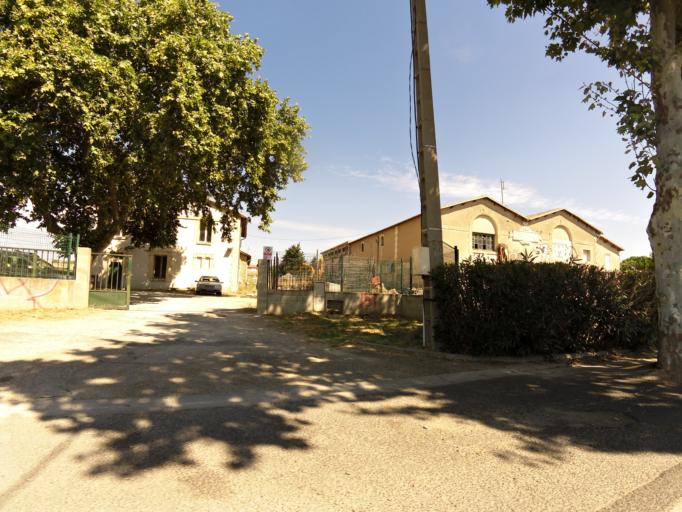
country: FR
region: Languedoc-Roussillon
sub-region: Departement de l'Herault
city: Lunel-Viel
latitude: 43.6773
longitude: 4.0866
